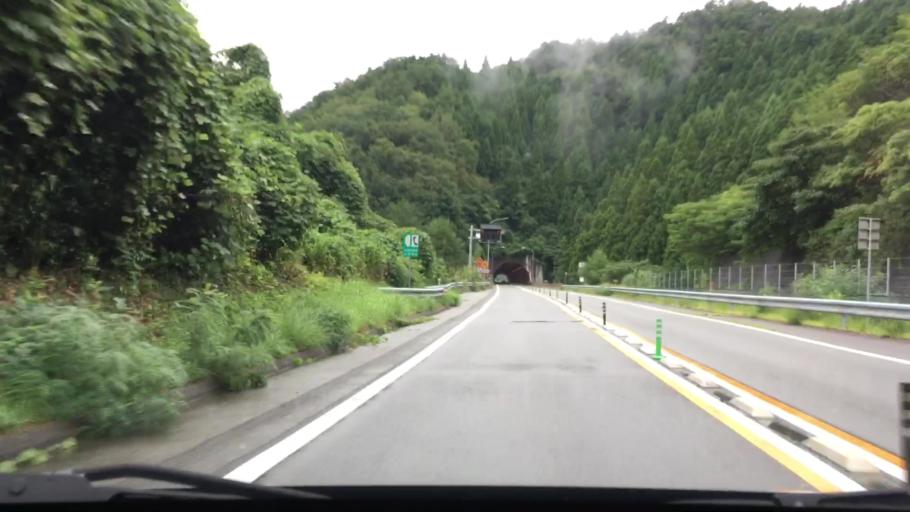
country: JP
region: Hyogo
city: Toyooka
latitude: 35.2571
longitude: 134.7945
